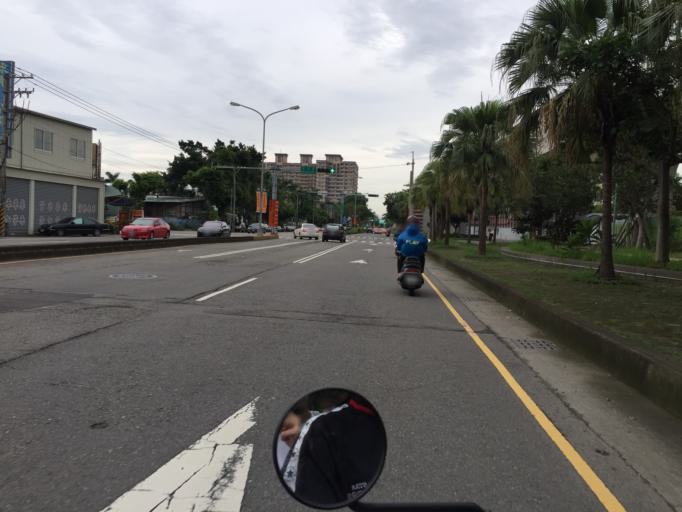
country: TW
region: Taiwan
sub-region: Taichung City
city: Taichung
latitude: 24.1582
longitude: 120.6993
